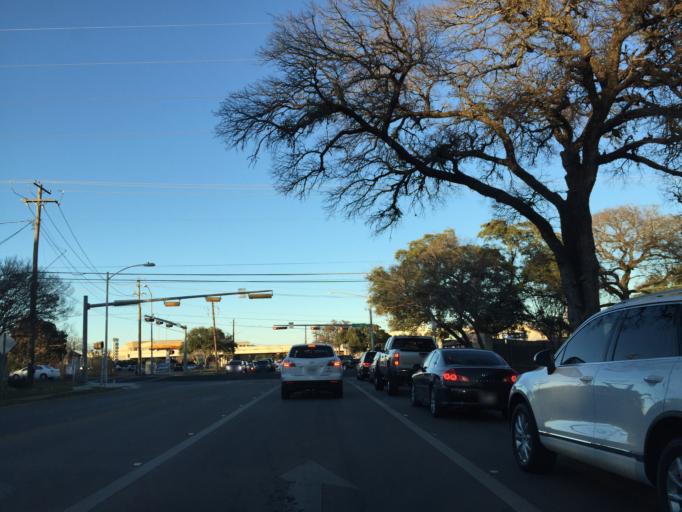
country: US
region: Texas
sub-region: Williamson County
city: Jollyville
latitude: 30.4272
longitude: -97.7604
